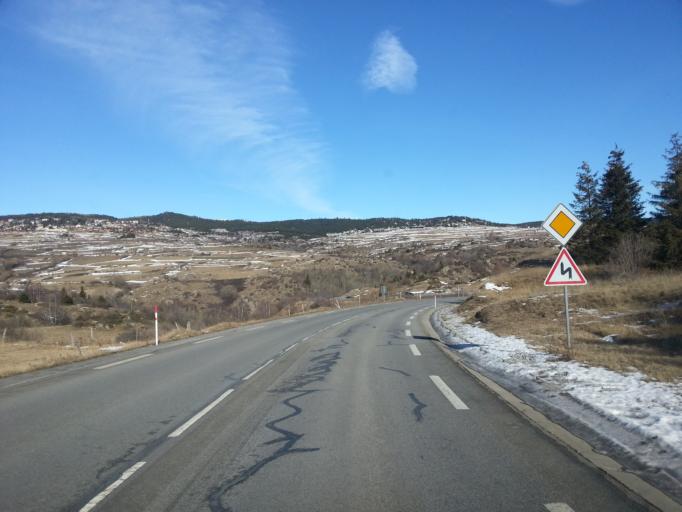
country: ES
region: Catalonia
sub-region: Provincia de Girona
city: Llivia
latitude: 42.4810
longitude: 2.0568
